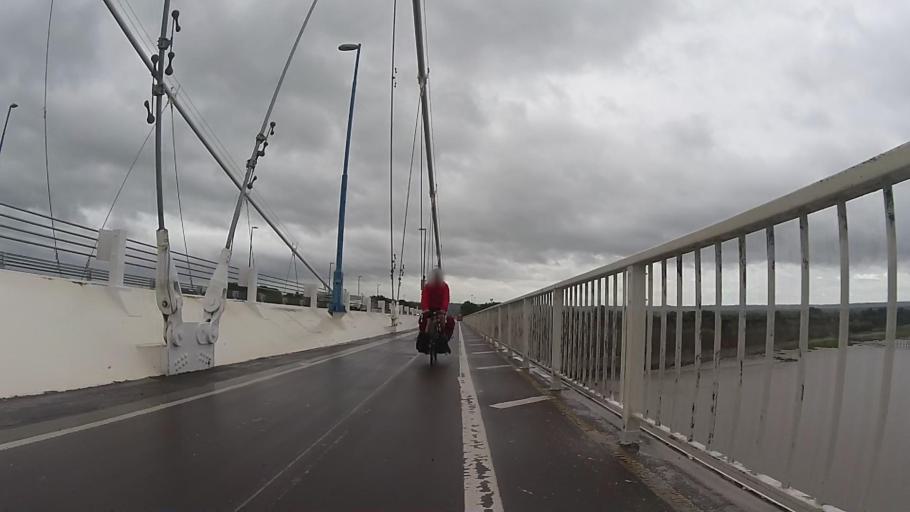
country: GB
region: England
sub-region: South Gloucestershire
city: Severn Beach
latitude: 51.6065
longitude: -2.6316
